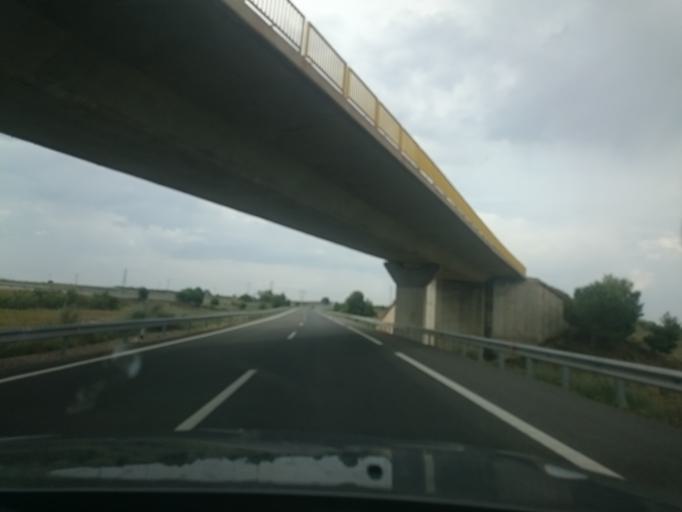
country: ES
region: Navarre
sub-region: Provincia de Navarra
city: Corella
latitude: 42.0964
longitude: -1.7217
